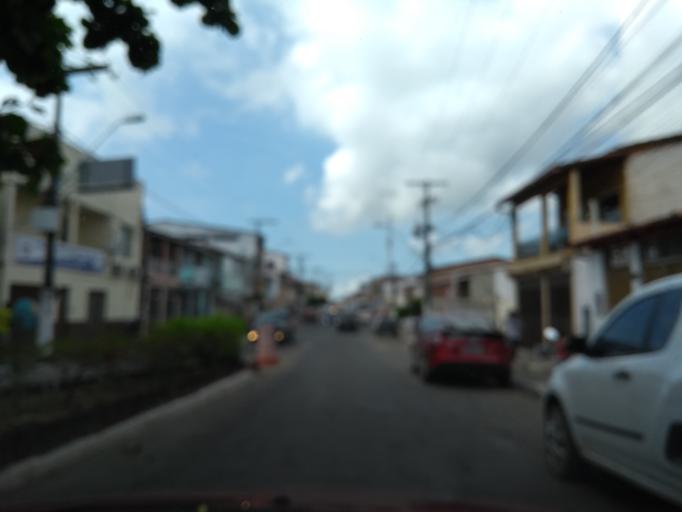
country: BR
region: Bahia
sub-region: Sao Francisco Do Conde
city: Sao Francisco do Conde
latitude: -12.6234
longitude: -38.6745
